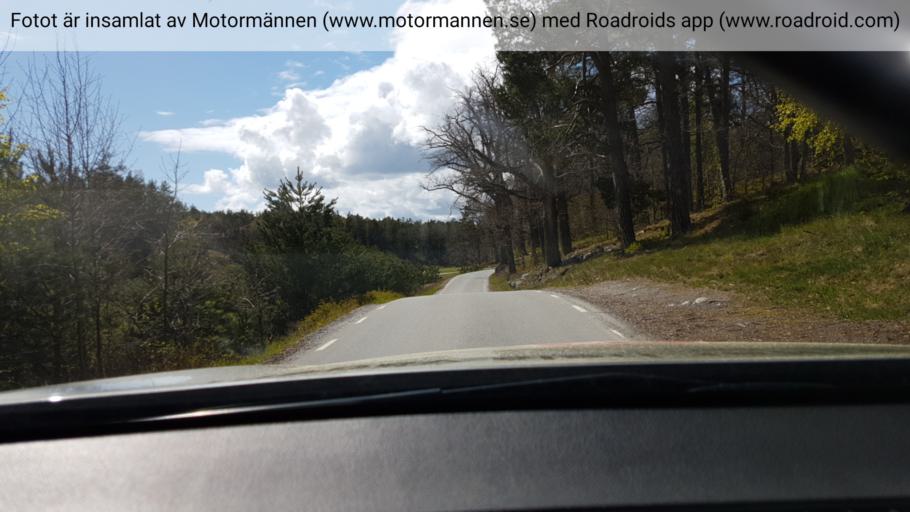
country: SE
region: Stockholm
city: Dalaro
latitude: 59.1651
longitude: 18.4510
